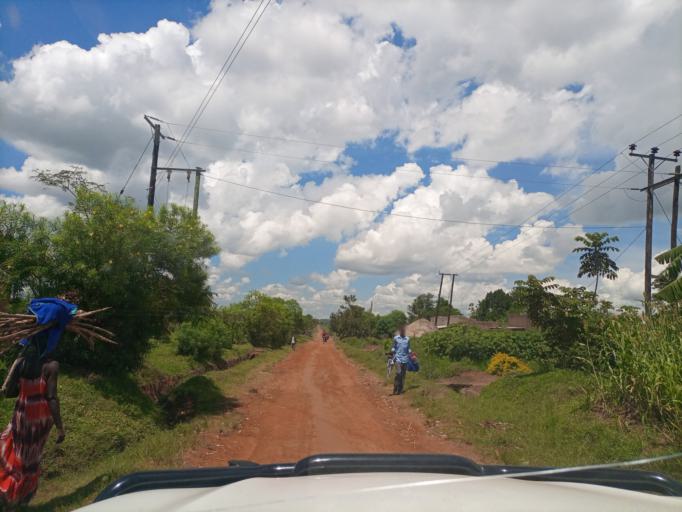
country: UG
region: Eastern Region
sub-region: Tororo District
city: Tororo
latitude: 0.6440
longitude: 33.9951
